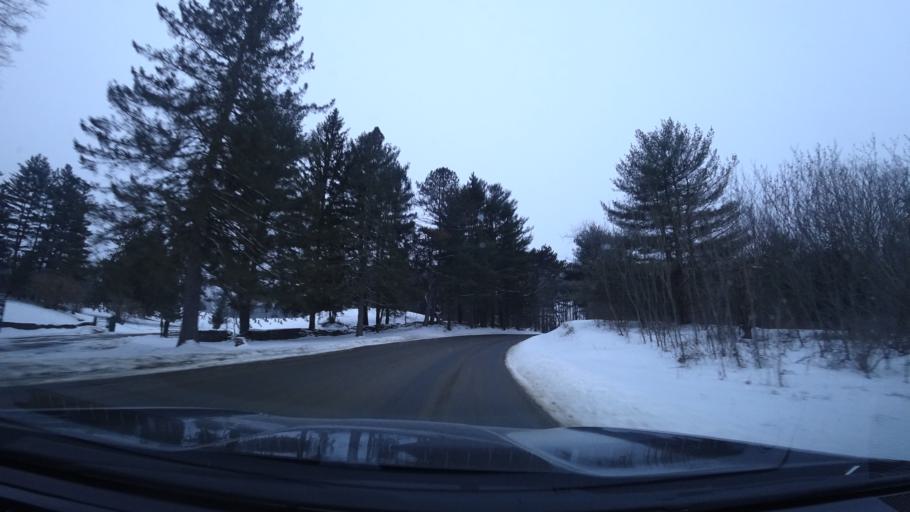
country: US
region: New York
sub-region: Washington County
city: Cambridge
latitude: 43.1628
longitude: -73.3451
